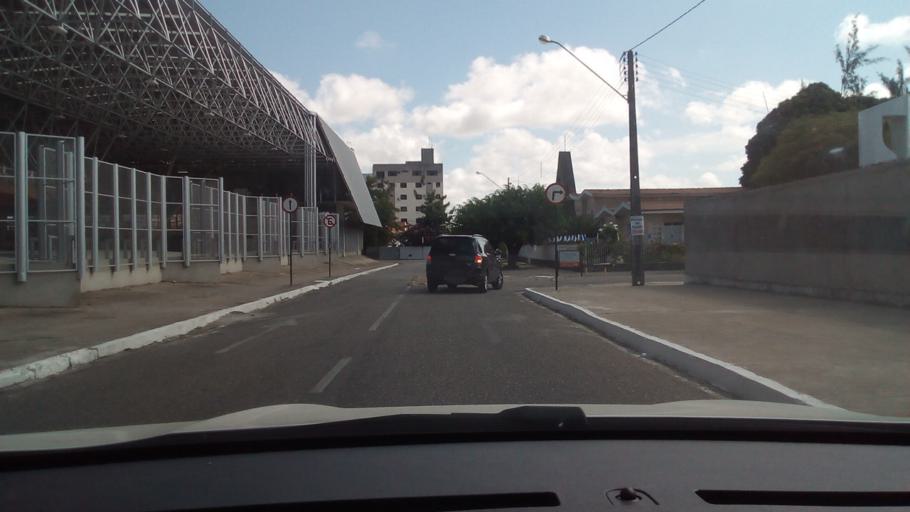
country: BR
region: Paraiba
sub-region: Joao Pessoa
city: Joao Pessoa
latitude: -7.1220
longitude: -34.8442
